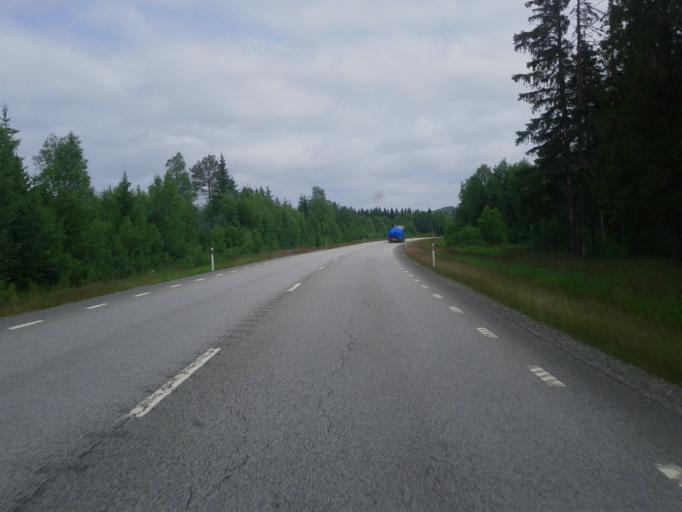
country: SE
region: Vaesterbotten
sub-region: Robertsfors Kommun
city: Robertsfors
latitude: 64.2898
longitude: 21.0762
